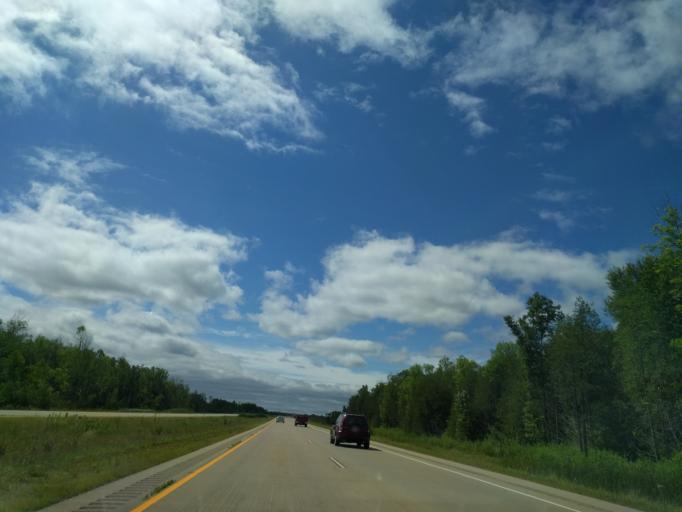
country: US
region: Wisconsin
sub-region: Oconto County
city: Oconto
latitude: 44.9134
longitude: -87.8781
